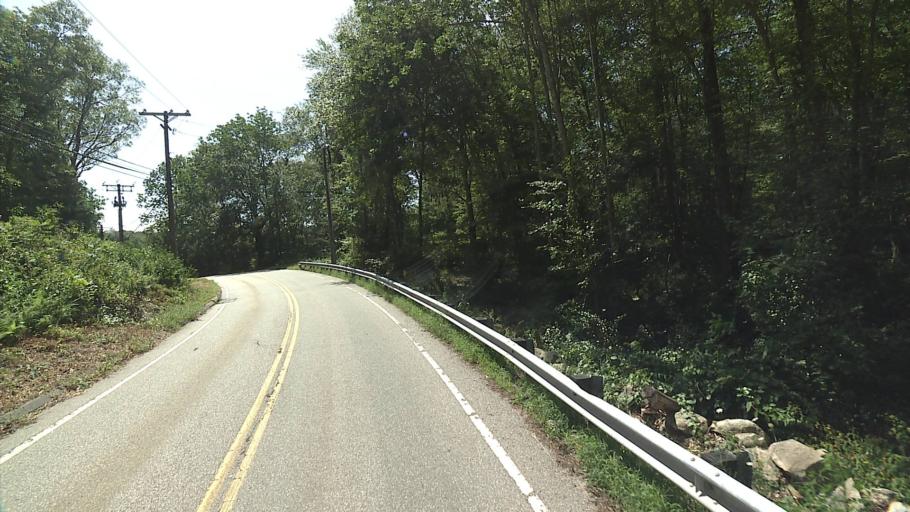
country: US
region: Connecticut
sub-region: New London County
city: Lisbon
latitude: 41.6080
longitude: -72.0218
